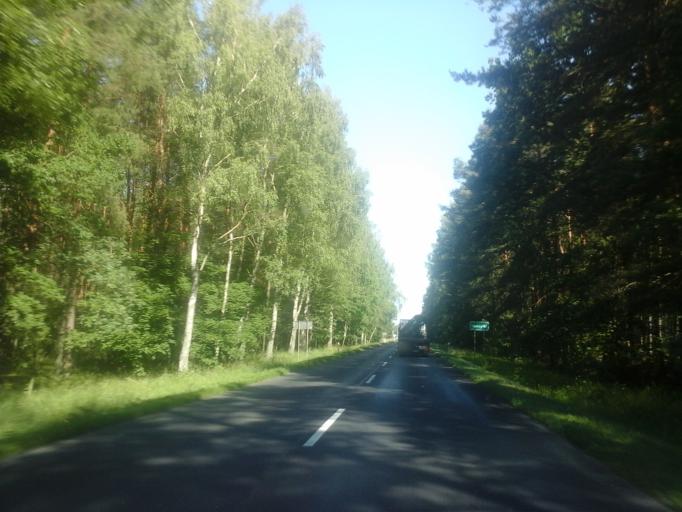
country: PL
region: West Pomeranian Voivodeship
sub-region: Powiat bialogardzki
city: Bialogard
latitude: 53.9719
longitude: 16.0424
